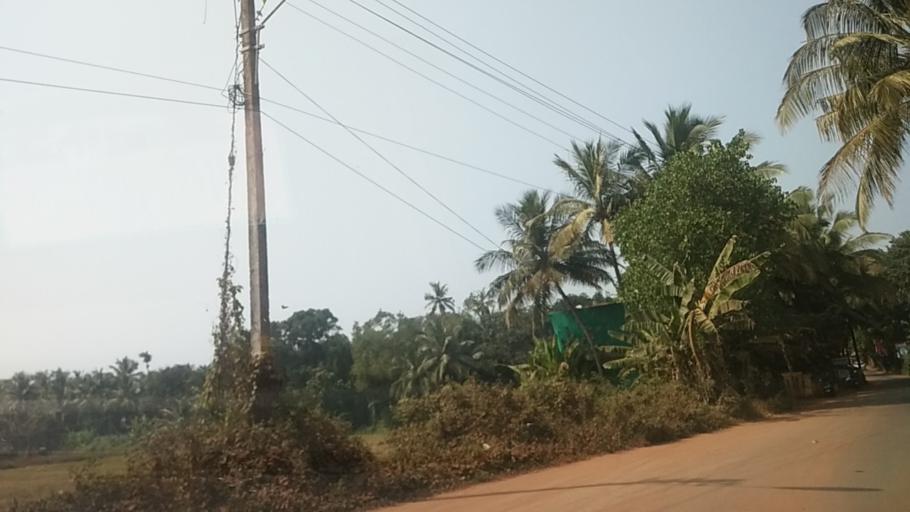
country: IN
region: Goa
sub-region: North Goa
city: Arambol
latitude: 15.6705
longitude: 73.7162
